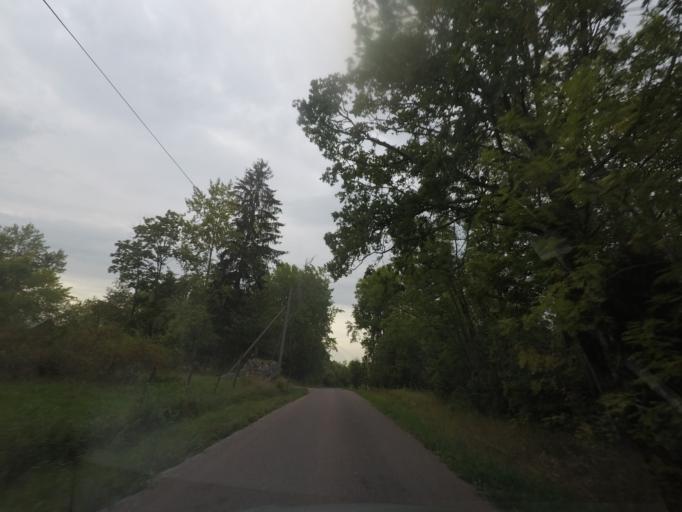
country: SE
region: Vaestmanland
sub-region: Hallstahammars Kommun
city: Kolback
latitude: 59.4954
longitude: 16.1897
